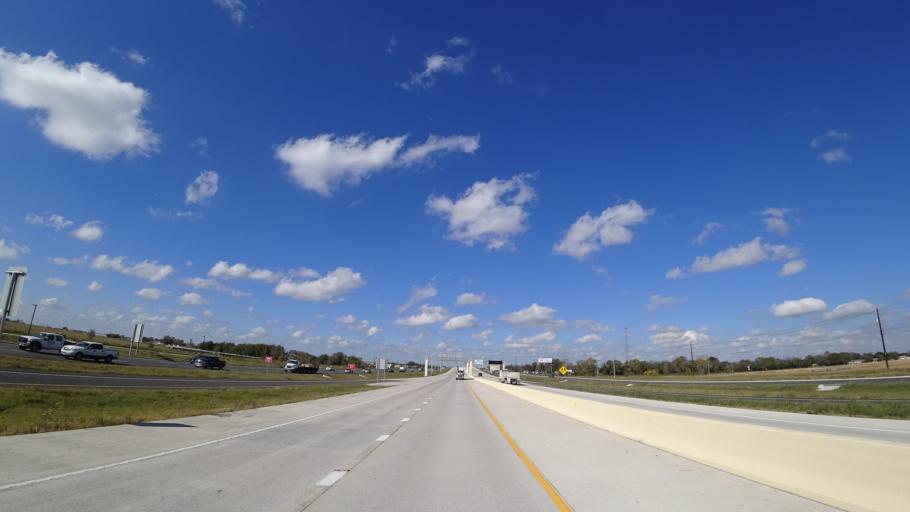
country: US
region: Texas
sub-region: Travis County
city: Hornsby Bend
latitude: 30.2003
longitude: -97.6346
